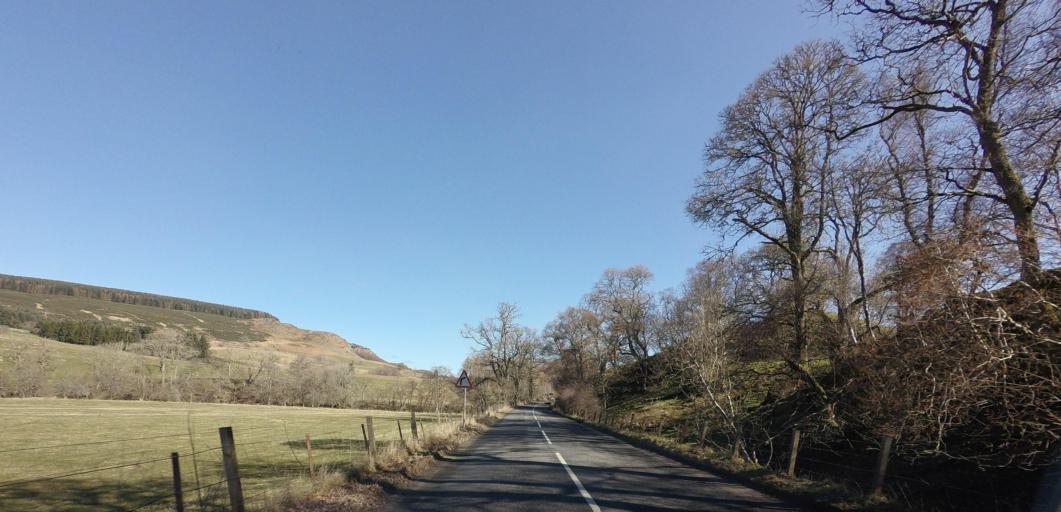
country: GB
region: Scotland
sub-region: Perth and Kinross
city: Methven
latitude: 56.5452
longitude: -3.6491
